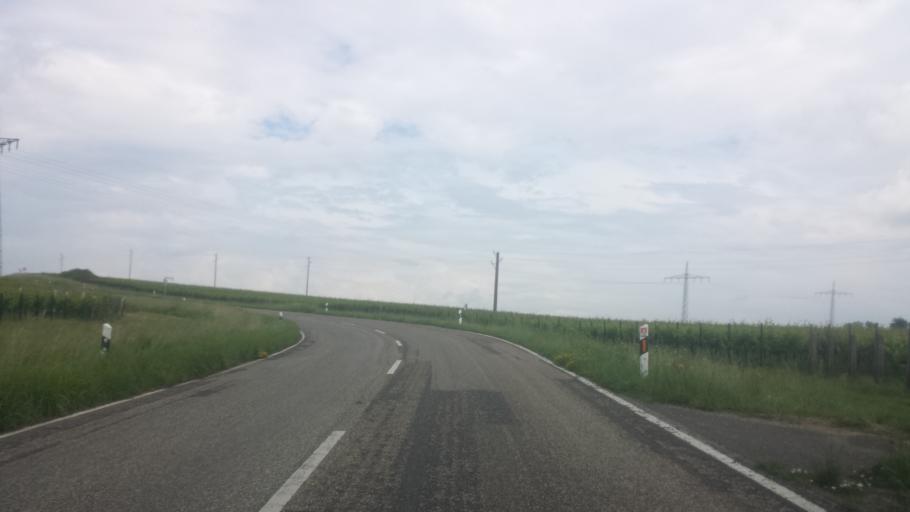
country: DE
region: Rheinland-Pfalz
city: Frankweiler
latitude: 49.2219
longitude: 8.0547
